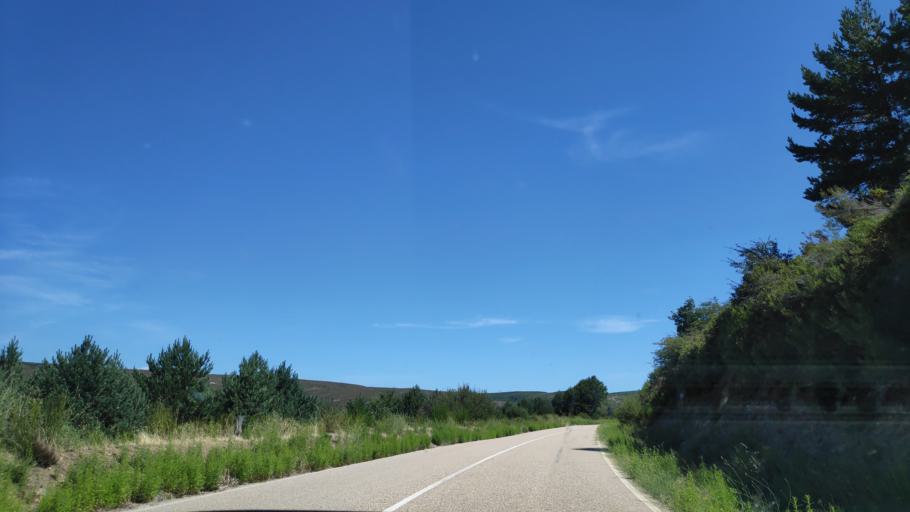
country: ES
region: Castille and Leon
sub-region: Provincia de Zamora
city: Requejo
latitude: 41.9904
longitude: -6.7047
